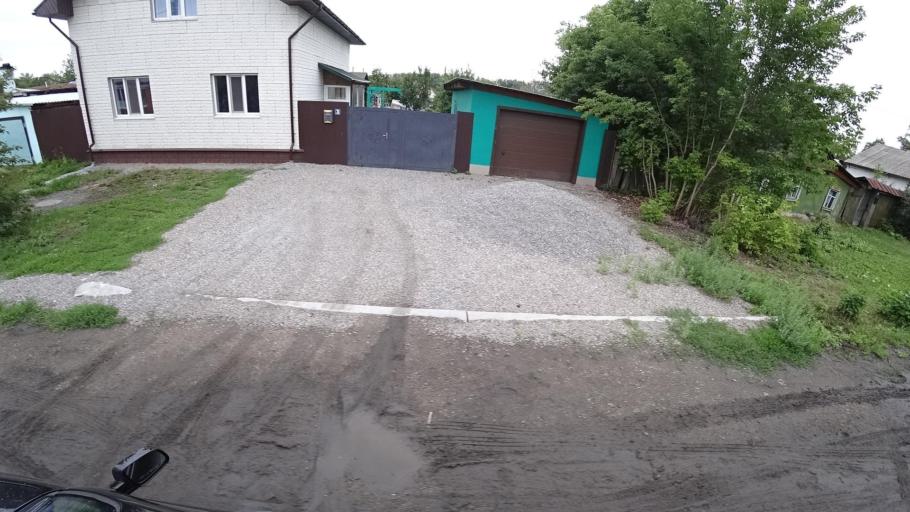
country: RU
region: Sverdlovsk
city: Kamyshlov
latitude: 56.8469
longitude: 62.7644
